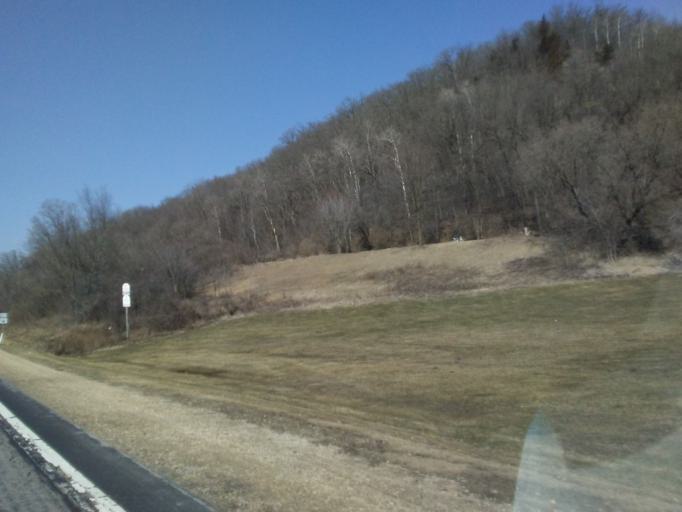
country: US
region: Wisconsin
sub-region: Vernon County
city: Viroqua
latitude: 43.4462
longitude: -90.7740
